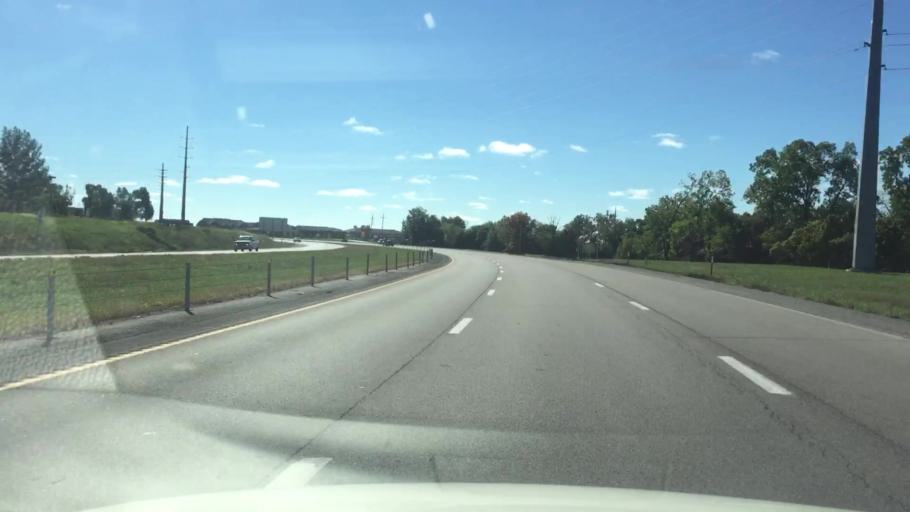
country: US
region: Missouri
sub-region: Boone County
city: Columbia
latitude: 38.9096
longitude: -92.2936
